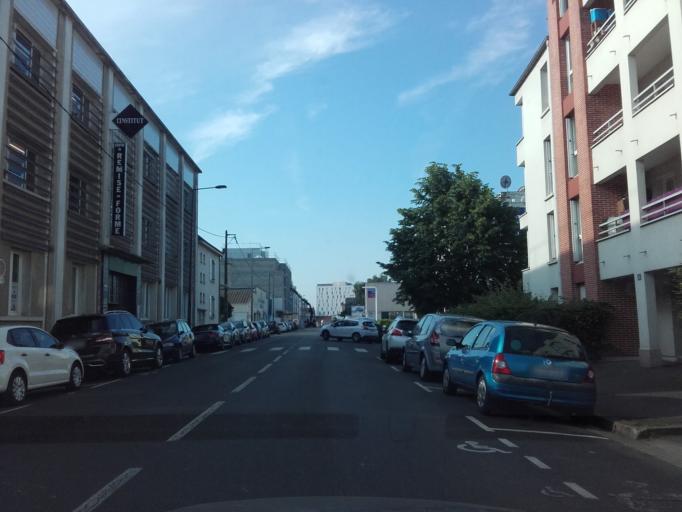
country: FR
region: Centre
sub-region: Departement d'Indre-et-Loire
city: Tours
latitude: 47.3791
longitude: 0.6775
